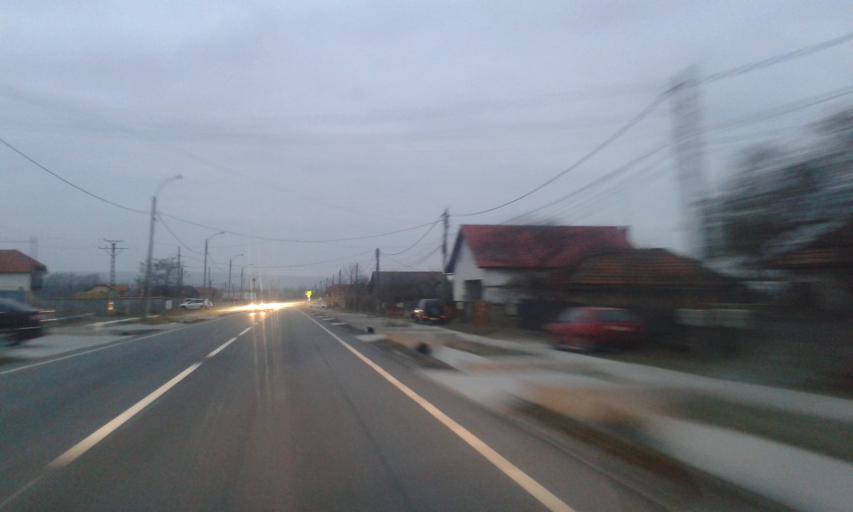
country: RO
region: Gorj
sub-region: Comuna Bumbesti-Jiu
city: Bumbesti-Jiu
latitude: 45.1723
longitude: 23.3814
